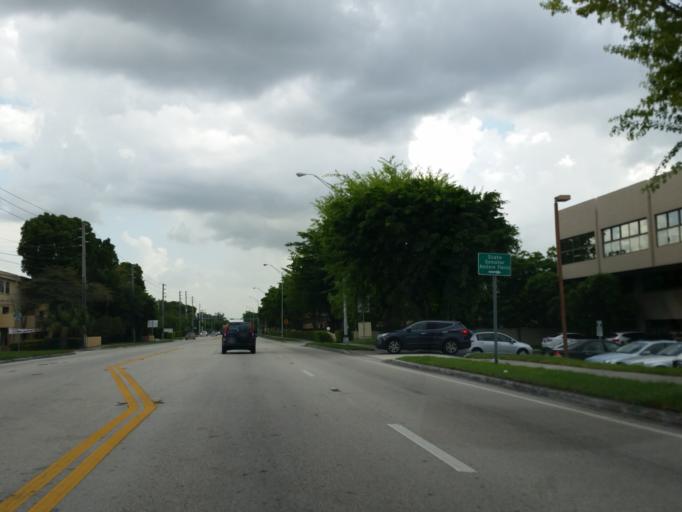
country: US
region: Florida
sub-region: Miami-Dade County
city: Sunset
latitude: 25.6881
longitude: -80.3659
